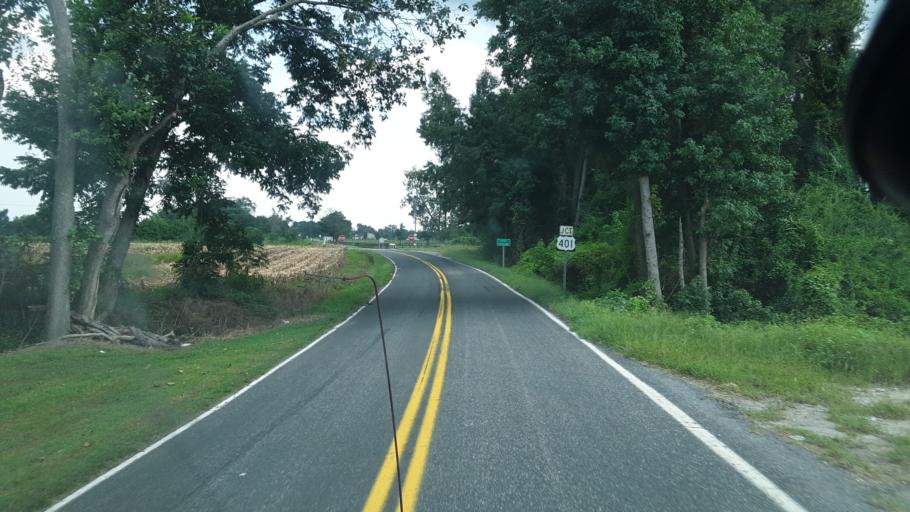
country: US
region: South Carolina
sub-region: Lee County
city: Bishopville
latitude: 34.1413
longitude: -80.1149
